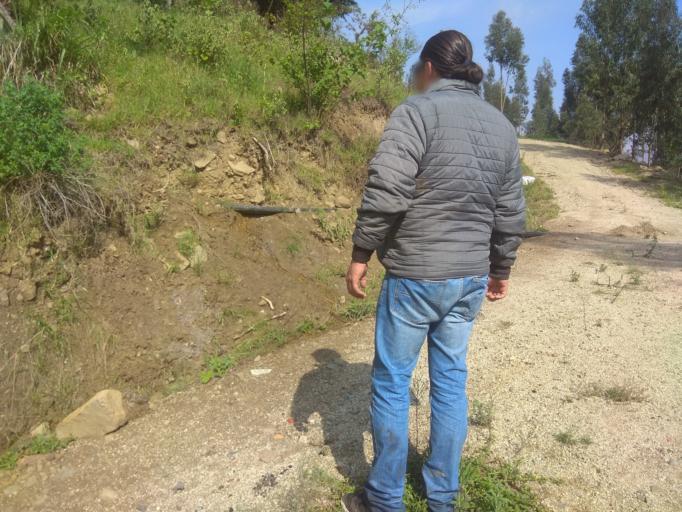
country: CO
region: Boyaca
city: Socha Viejo
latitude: 5.9809
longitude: -72.7062
